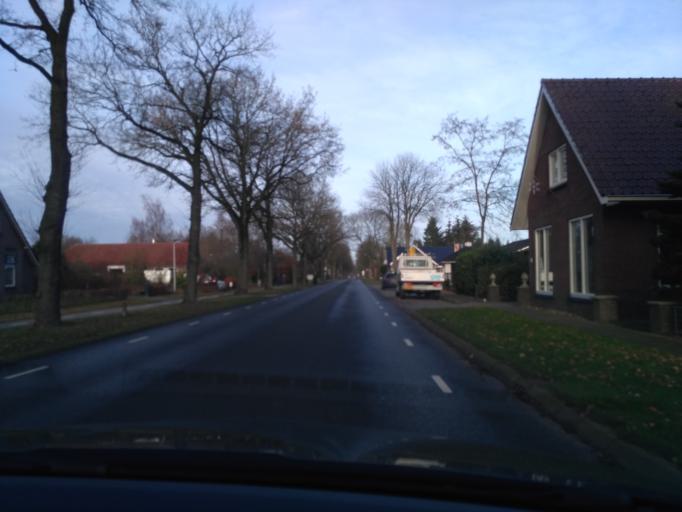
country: NL
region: Drenthe
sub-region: Gemeente Borger-Odoorn
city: Borger
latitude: 52.8563
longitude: 6.7504
